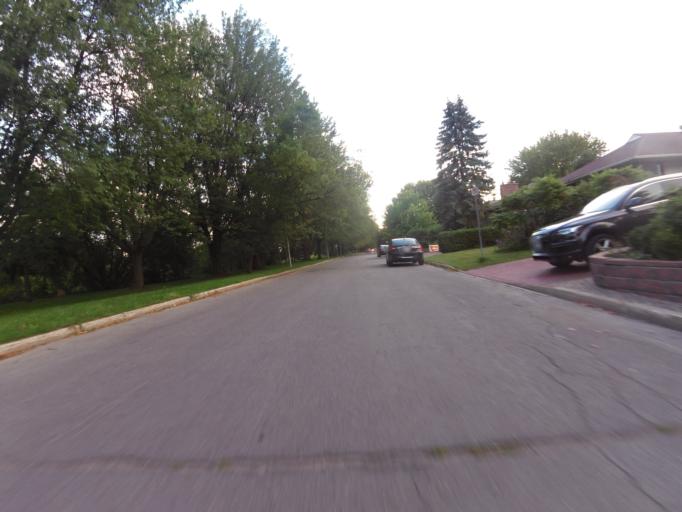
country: CA
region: Ontario
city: Ottawa
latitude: 45.3994
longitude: -75.6725
